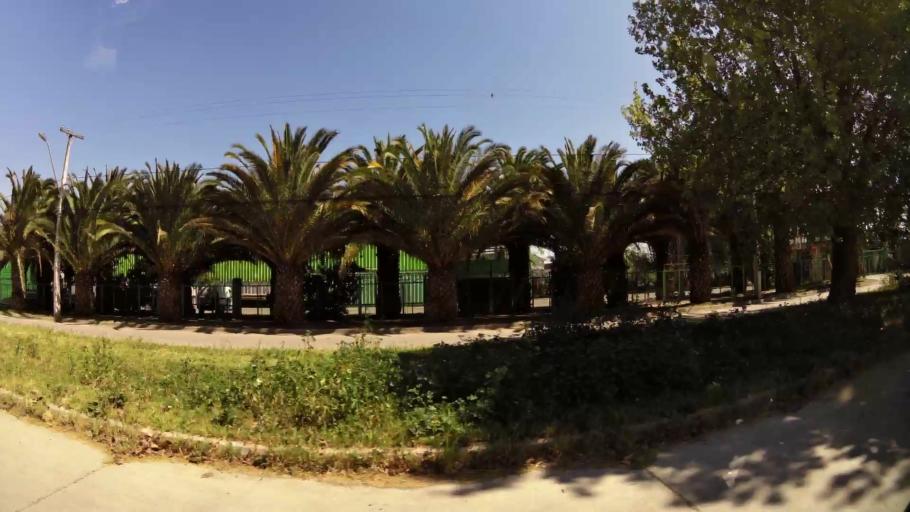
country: CL
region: Santiago Metropolitan
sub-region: Provincia de Santiago
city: Lo Prado
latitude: -33.3785
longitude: -70.7443
